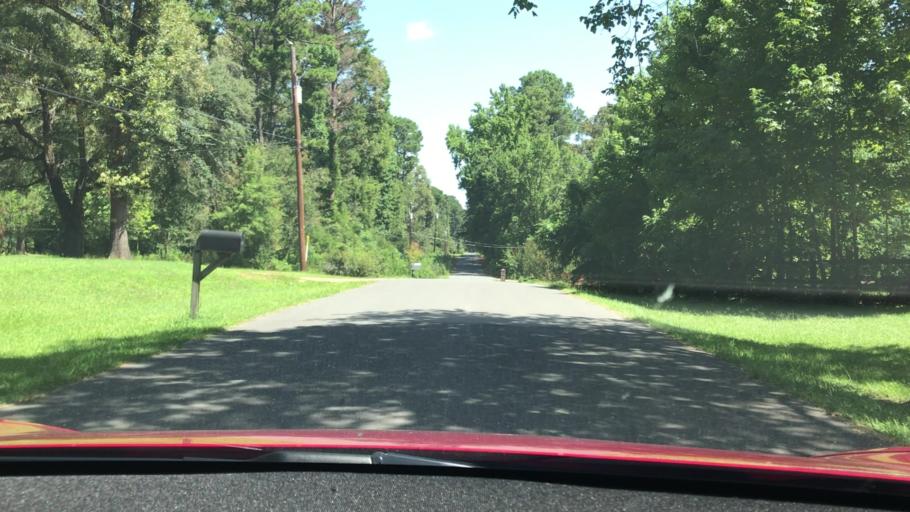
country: US
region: Louisiana
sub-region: De Soto Parish
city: Stonewall
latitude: 32.3412
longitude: -93.7085
